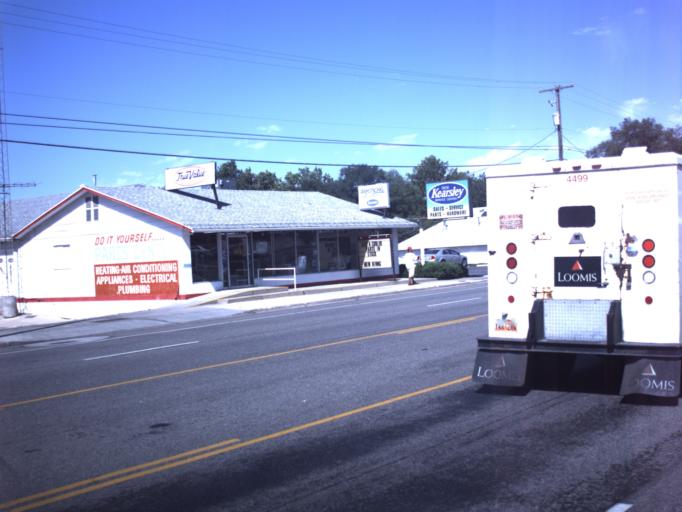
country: US
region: Utah
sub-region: Davis County
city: Clearfield
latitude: 41.1063
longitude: -112.0183
